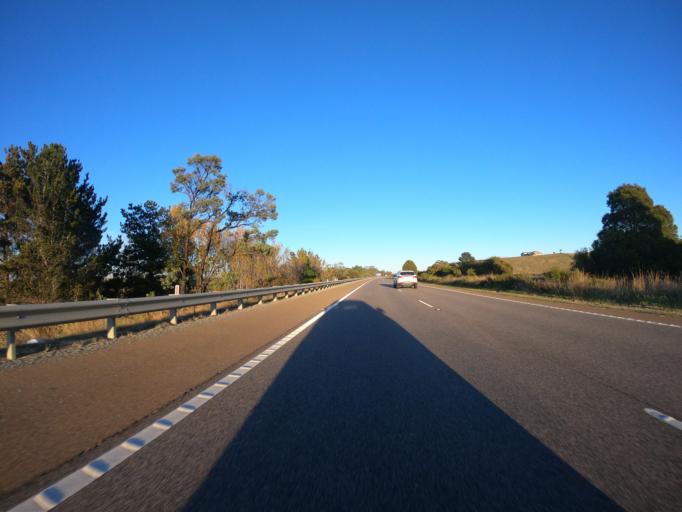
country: AU
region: New South Wales
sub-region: Goulburn Mulwaree
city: Goulburn
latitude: -34.8940
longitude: 149.5139
